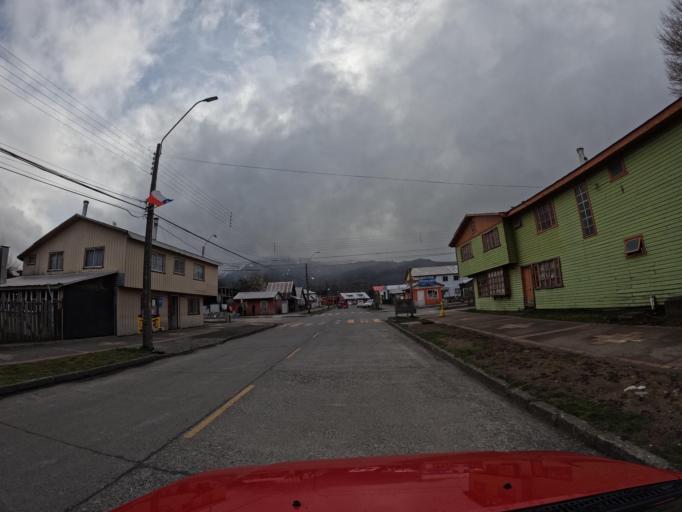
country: AR
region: Neuquen
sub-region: Departamento de Loncopue
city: Loncopue
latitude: -38.4570
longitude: -71.3677
